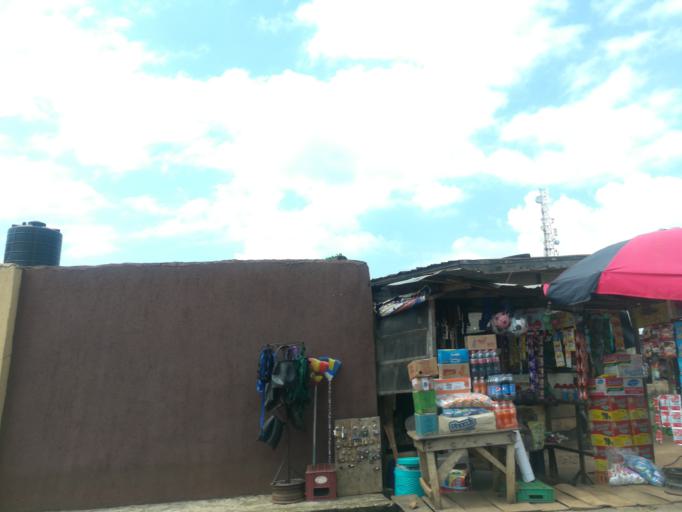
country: NG
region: Oyo
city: Egbeda
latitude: 7.4225
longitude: 3.9975
